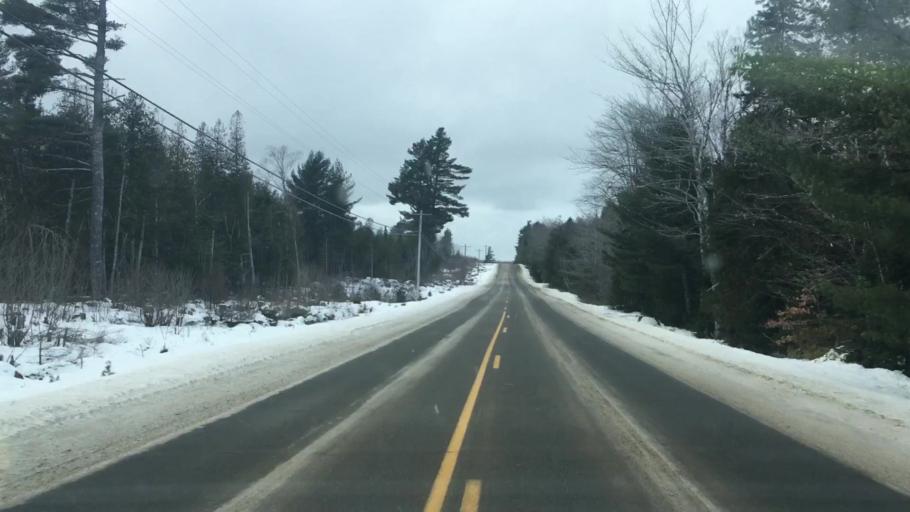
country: US
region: Maine
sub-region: Washington County
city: Calais
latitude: 45.0081
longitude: -67.4058
